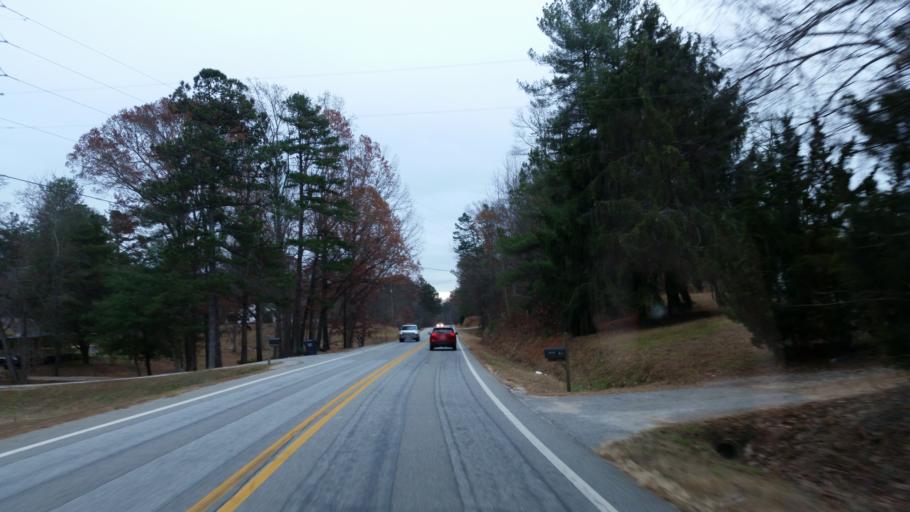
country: US
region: Georgia
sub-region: Dawson County
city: Dawsonville
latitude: 34.4374
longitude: -84.0798
